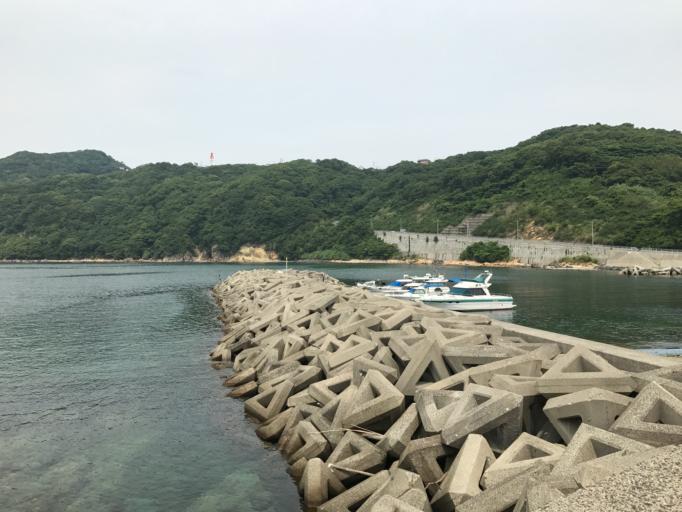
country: JP
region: Nagasaki
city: Nagasaki-shi
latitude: 32.7322
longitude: 129.8277
